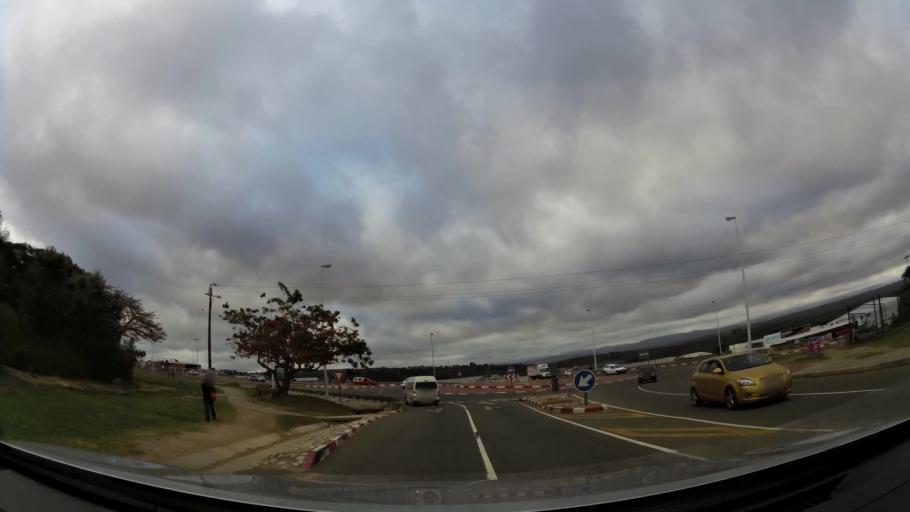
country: ZA
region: Western Cape
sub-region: Eden District Municipality
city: Plettenberg Bay
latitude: -34.0505
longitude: 23.3572
